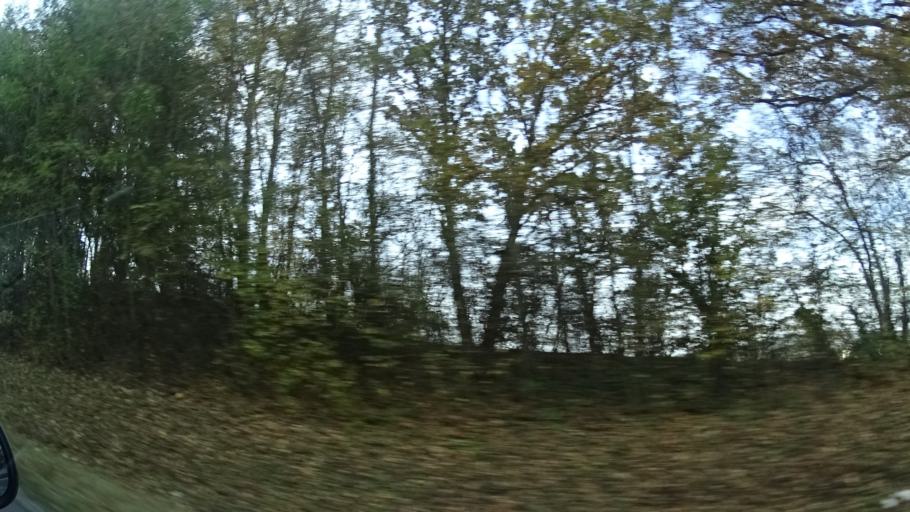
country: DE
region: Baden-Wuerttemberg
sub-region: Karlsruhe Region
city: Obrigheim
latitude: 49.3474
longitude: 9.0955
